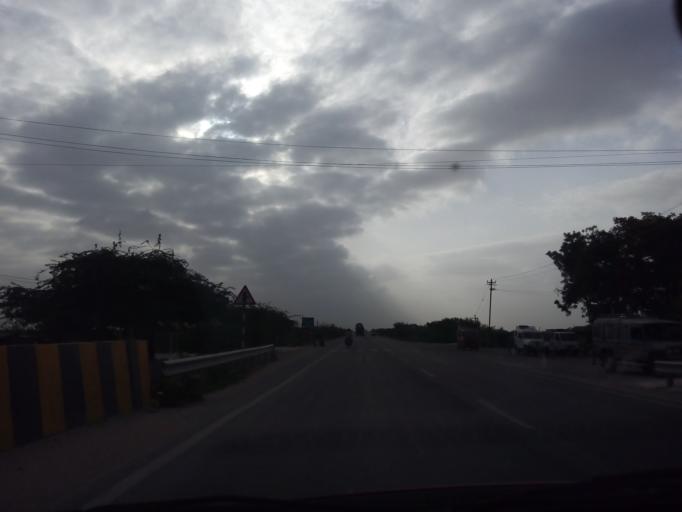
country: IN
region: Gujarat
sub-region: Kachchh
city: Anjar
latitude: 23.2638
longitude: 69.9175
